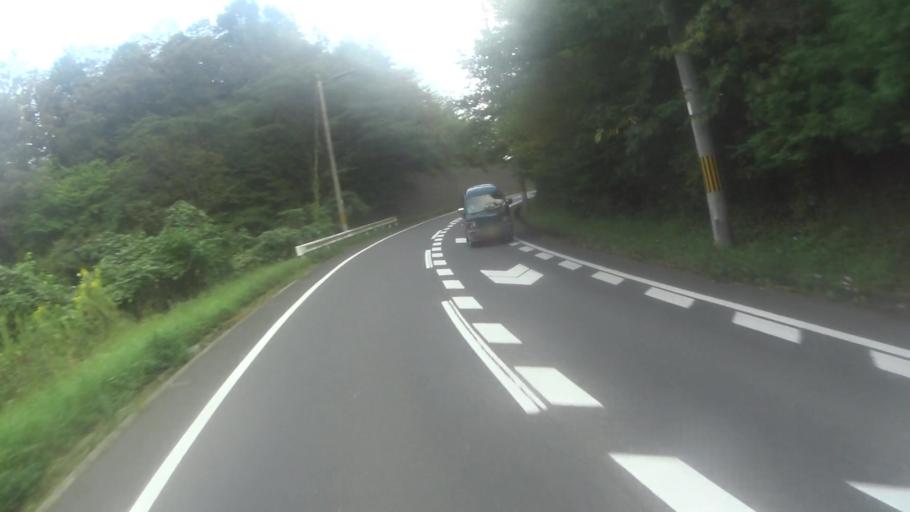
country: JP
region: Kyoto
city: Miyazu
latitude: 35.5281
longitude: 135.0927
